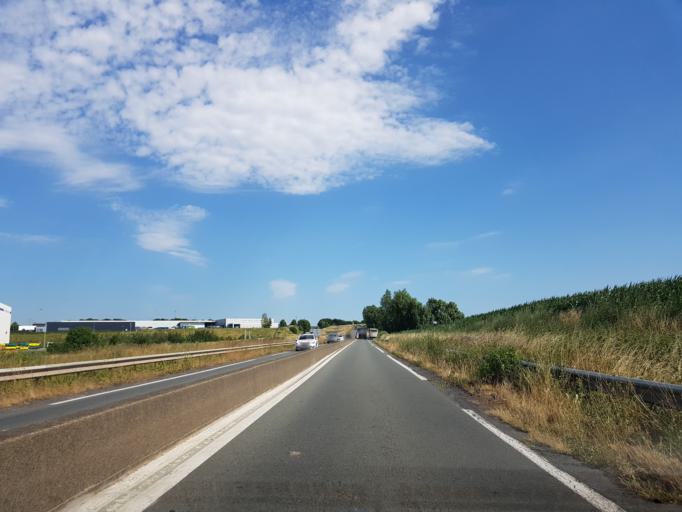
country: FR
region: Nord-Pas-de-Calais
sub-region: Departement du Nord
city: Onnaing
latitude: 50.3663
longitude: 3.6020
